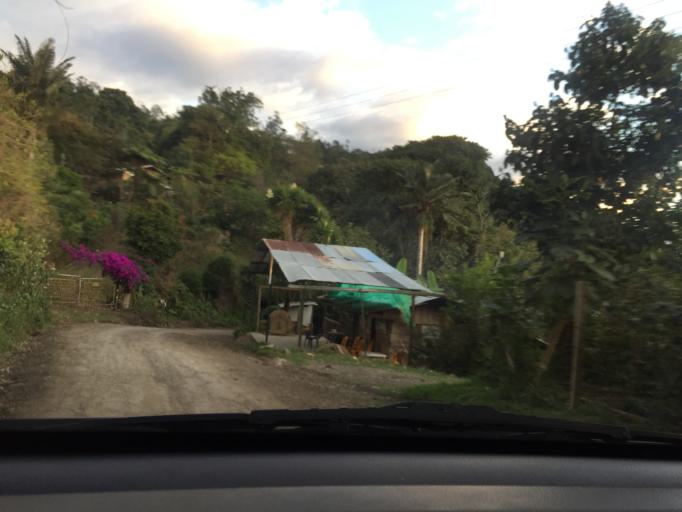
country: CO
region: Cundinamarca
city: Zipacon
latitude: 4.7073
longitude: -74.4052
